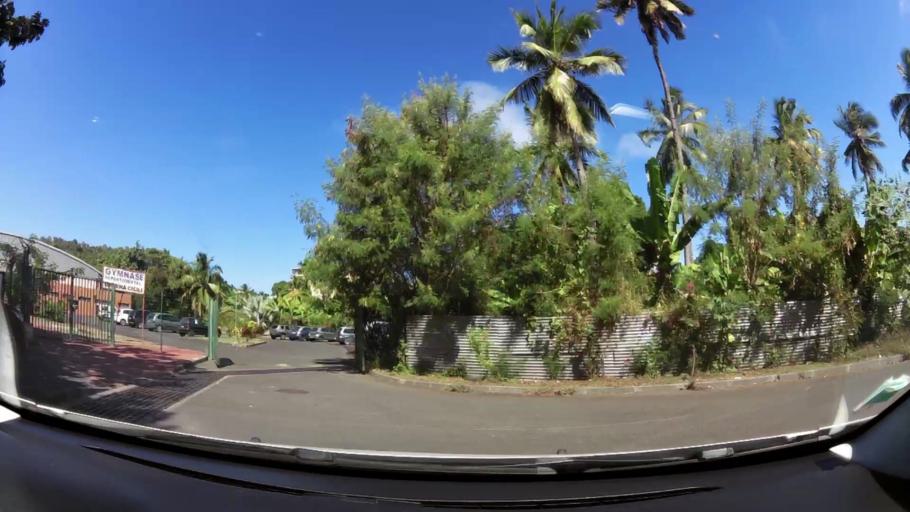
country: YT
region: Pamandzi
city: Pamandzi
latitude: -12.7855
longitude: 45.2797
